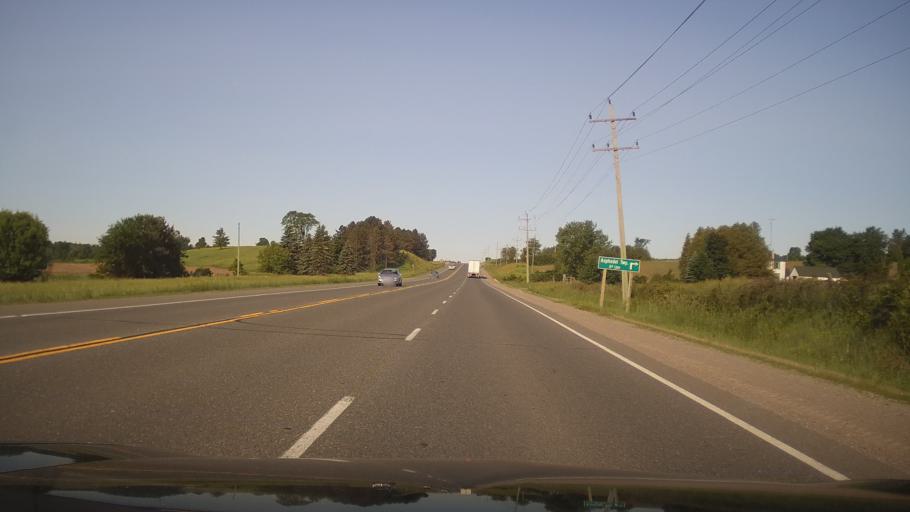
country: CA
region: Ontario
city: Peterborough
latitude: 44.3628
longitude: -78.0161
